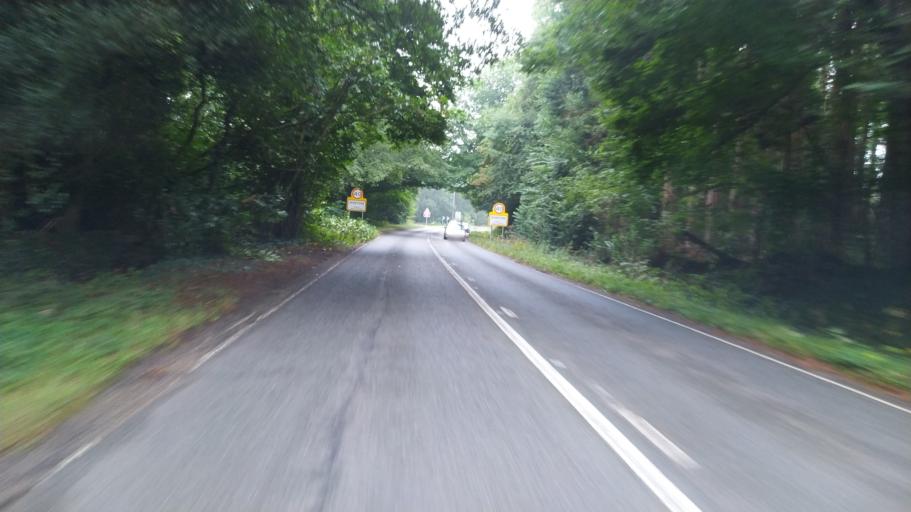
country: GB
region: England
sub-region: Hampshire
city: New Milton
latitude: 50.7647
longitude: -1.6978
